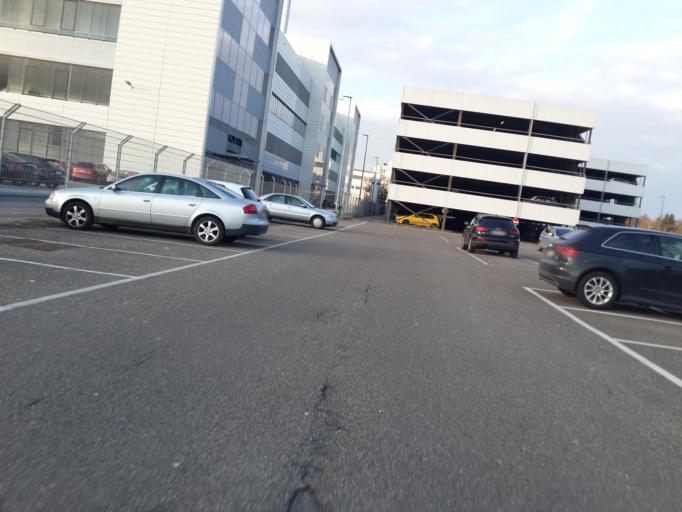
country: DE
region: Baden-Wuerttemberg
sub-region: Regierungsbezirk Stuttgart
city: Neckarsulm
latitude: 49.1967
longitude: 9.2248
